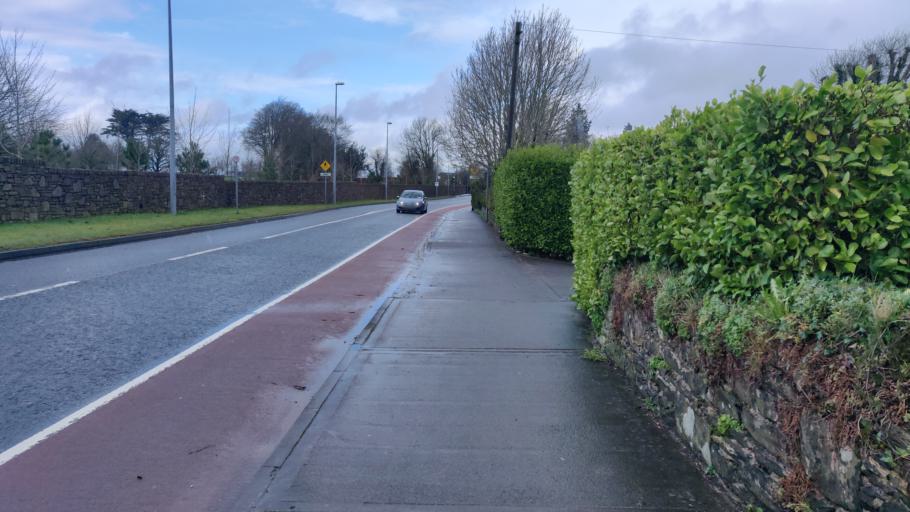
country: IE
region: Munster
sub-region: County Cork
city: Carrigaline
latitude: 51.8682
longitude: -8.4168
